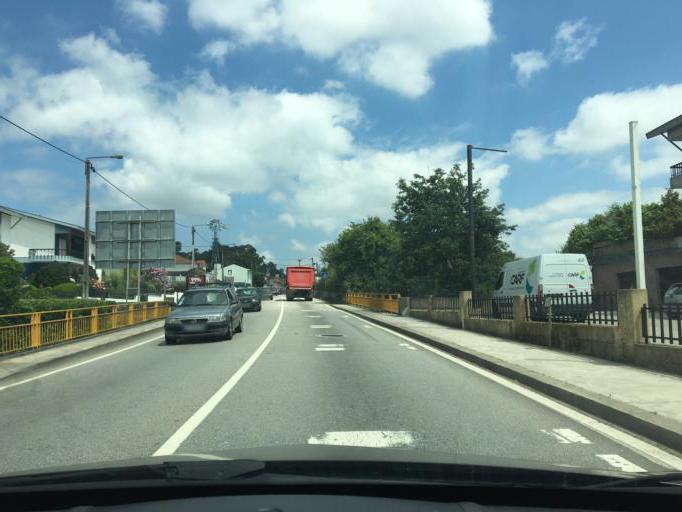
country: PT
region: Porto
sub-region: Maia
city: Anta
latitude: 41.2824
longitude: -8.6055
